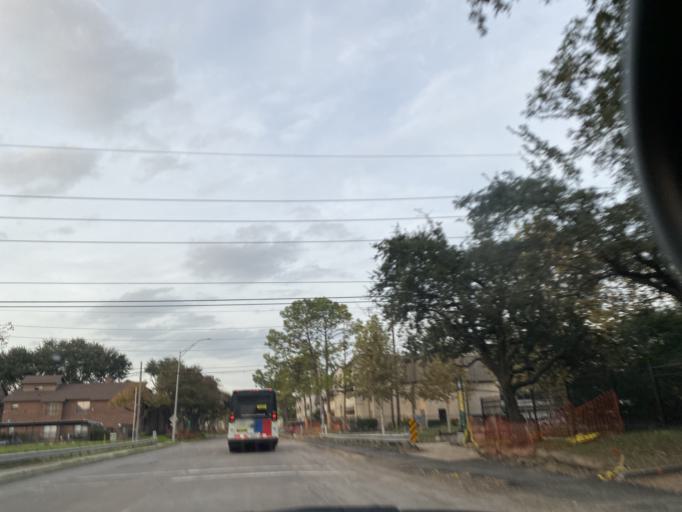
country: US
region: Texas
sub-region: Harris County
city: Bunker Hill Village
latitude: 29.7289
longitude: -95.5680
